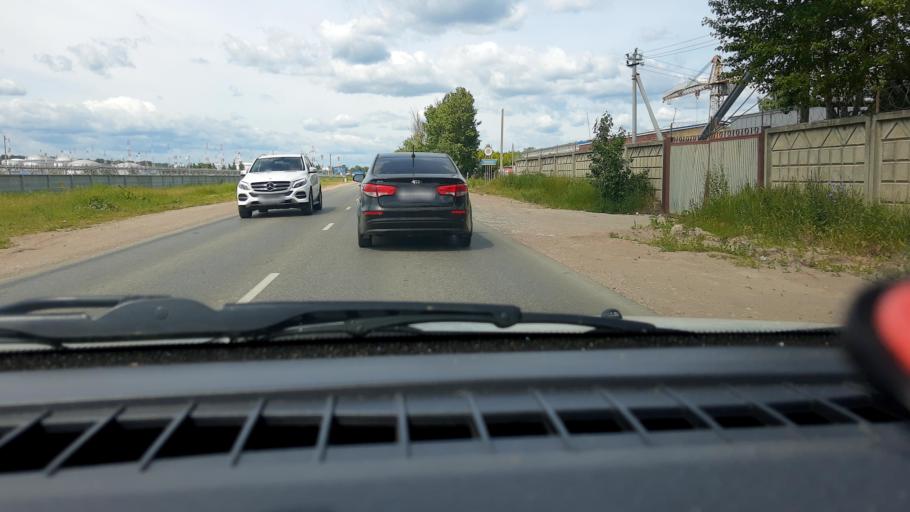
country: RU
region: Nizjnij Novgorod
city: Kstovo
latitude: 56.1224
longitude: 44.1336
